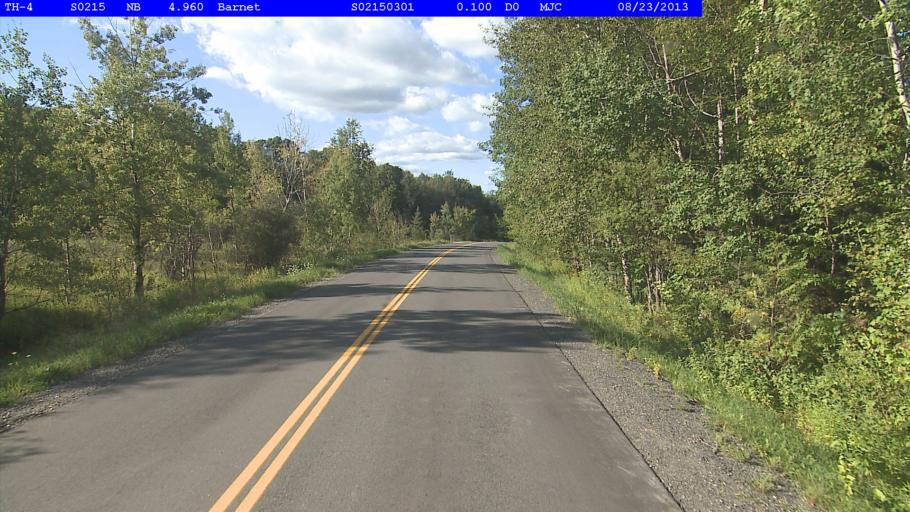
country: US
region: New Hampshire
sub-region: Grafton County
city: Woodsville
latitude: 44.2757
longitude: -72.1738
